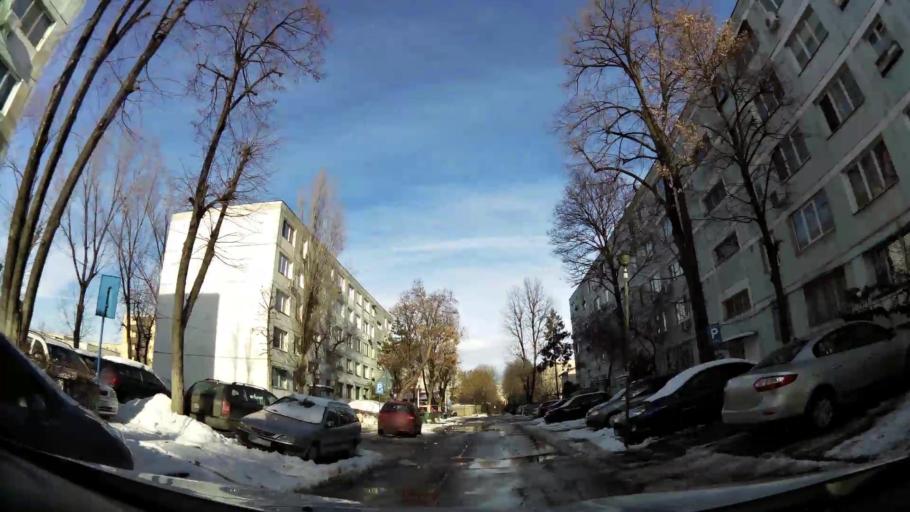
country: RO
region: Bucuresti
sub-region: Municipiul Bucuresti
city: Bucuresti
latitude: 44.3853
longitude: 26.0985
